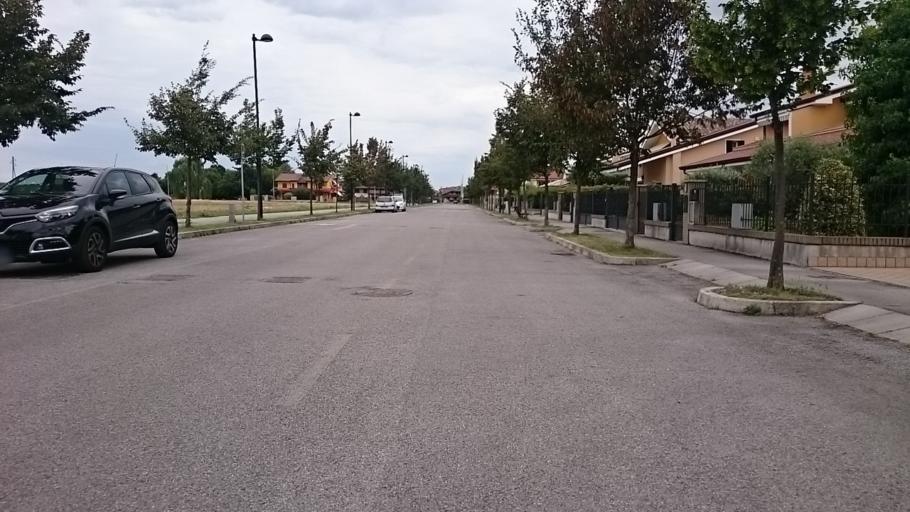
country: IT
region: Veneto
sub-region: Provincia di Padova
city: Masera di Padova
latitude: 45.3371
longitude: 11.8679
